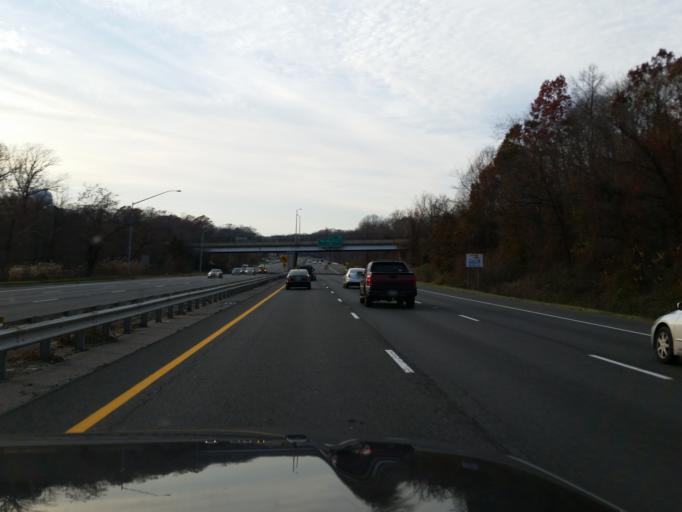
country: US
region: Maryland
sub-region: Anne Arundel County
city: Cape Saint Claire
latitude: 39.0270
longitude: -76.4471
